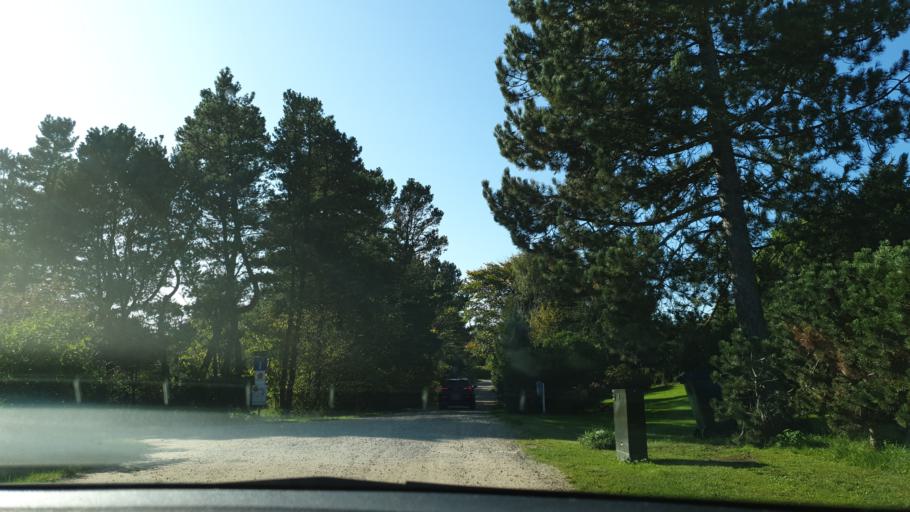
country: DK
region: Zealand
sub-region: Odsherred Kommune
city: Hojby
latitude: 55.9366
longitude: 11.6269
